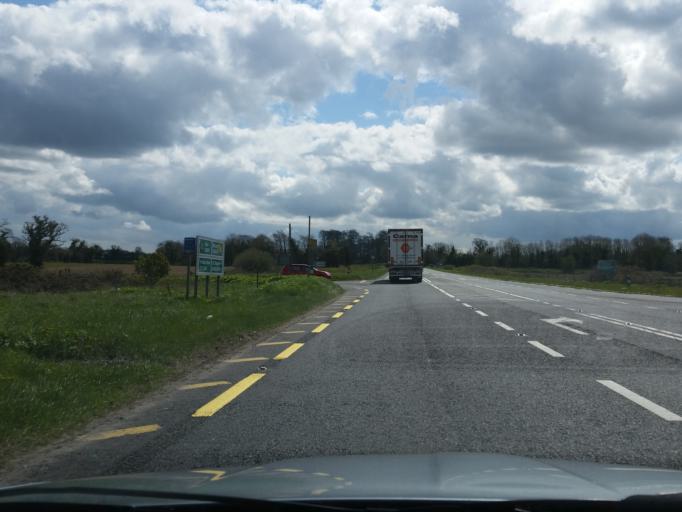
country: IE
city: Kentstown
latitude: 53.6029
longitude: -6.4718
